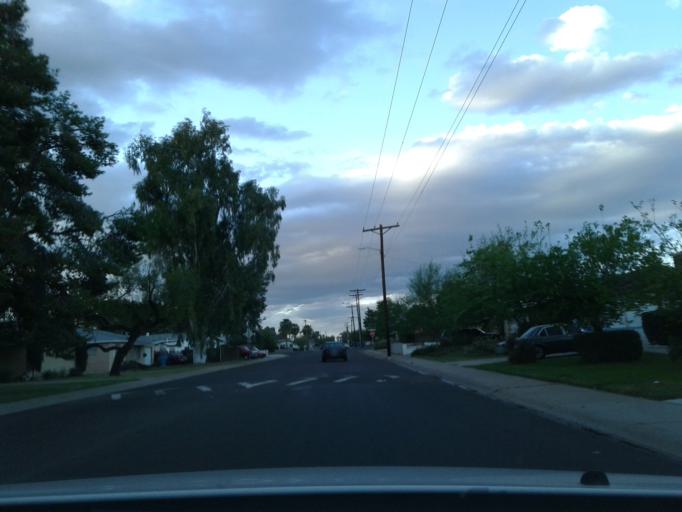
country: US
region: Arizona
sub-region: Maricopa County
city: Glendale
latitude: 33.5448
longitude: -112.1039
